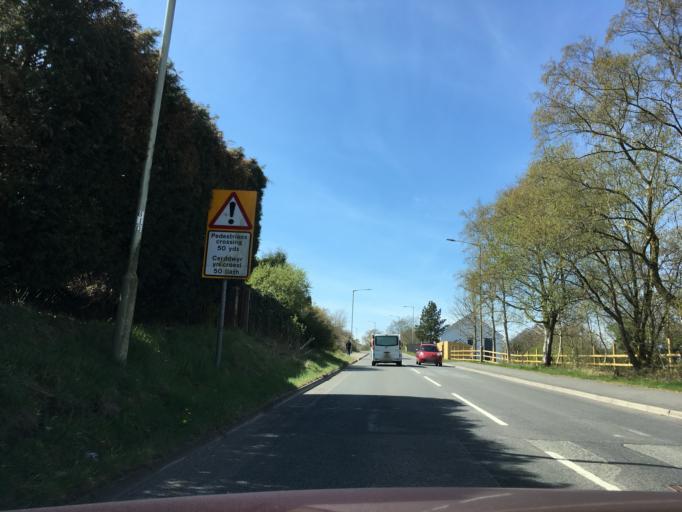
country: GB
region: Wales
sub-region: Merthyr Tydfil County Borough
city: Merthyr Tydfil
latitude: 51.7547
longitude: -3.4196
